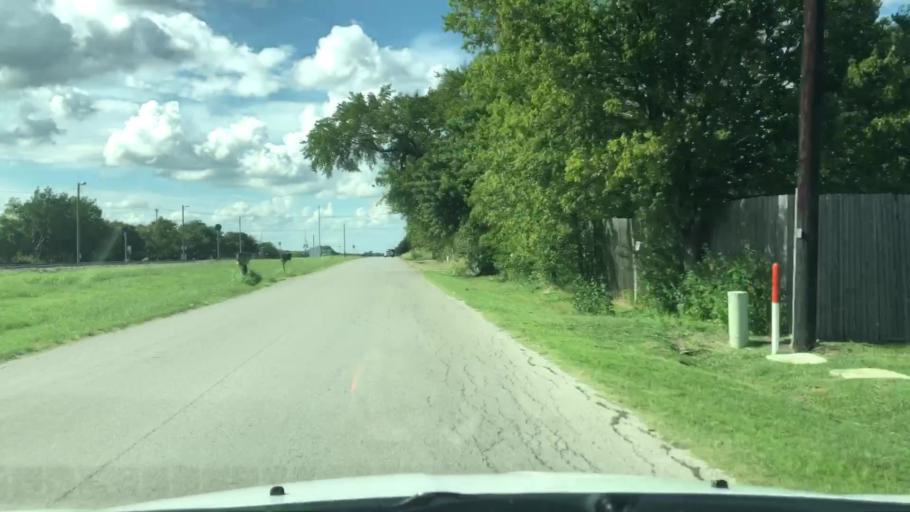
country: US
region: Texas
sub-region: Ellis County
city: Ennis
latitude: 32.3497
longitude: -96.6413
